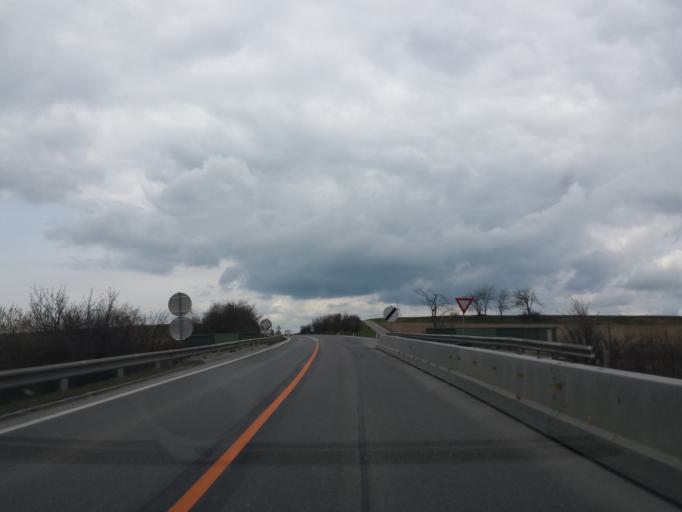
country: AT
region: Lower Austria
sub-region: Politischer Bezirk Krems
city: Gfohl
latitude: 48.5150
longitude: 15.5094
